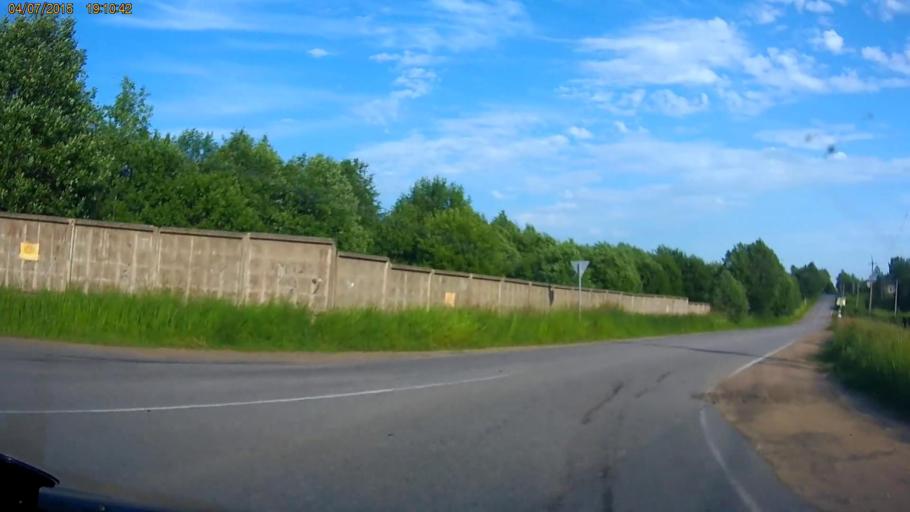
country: RU
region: Leningrad
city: Garbolovo
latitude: 60.3351
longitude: 30.4846
